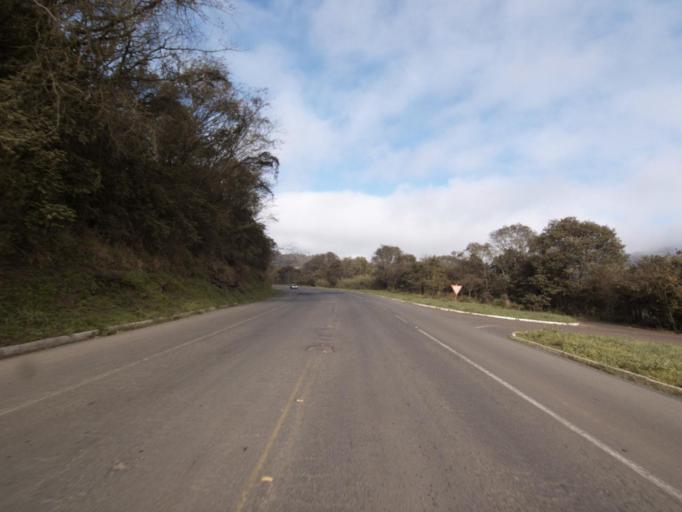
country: BR
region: Rio Grande do Sul
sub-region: Frederico Westphalen
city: Frederico Westphalen
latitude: -27.0291
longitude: -53.2347
